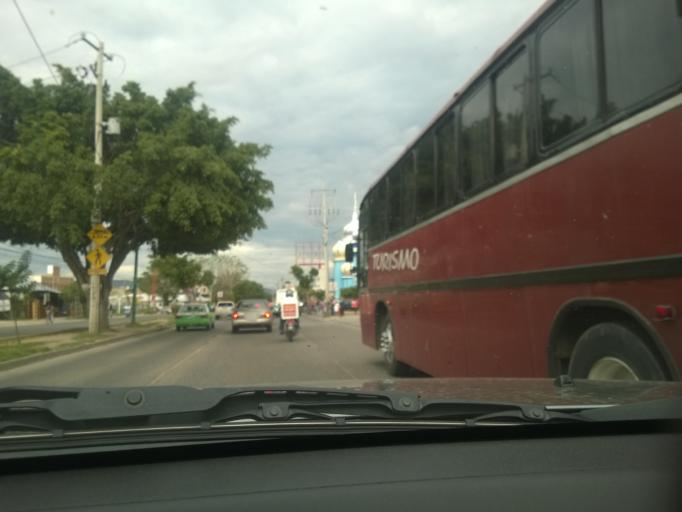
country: MX
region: Guanajuato
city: Leon
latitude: 21.1306
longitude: -101.6579
